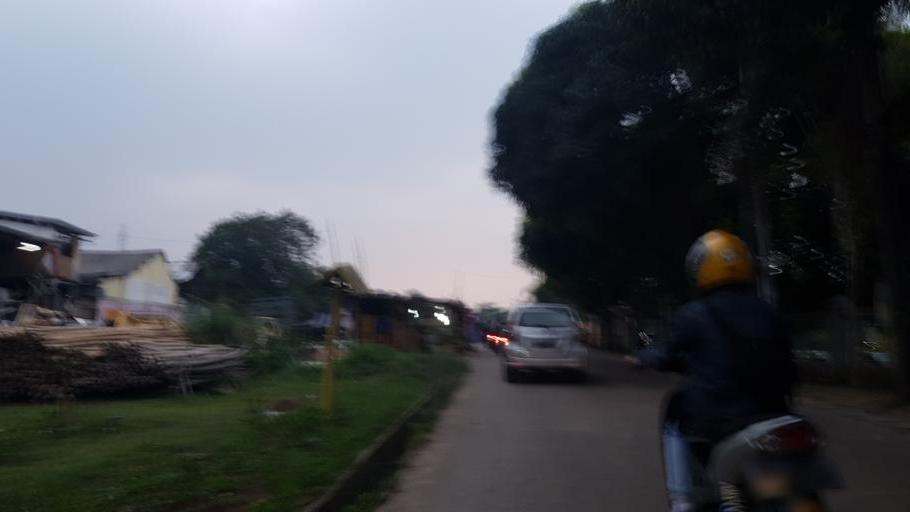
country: ID
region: West Java
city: Sawangan
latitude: -6.3643
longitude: 106.7926
